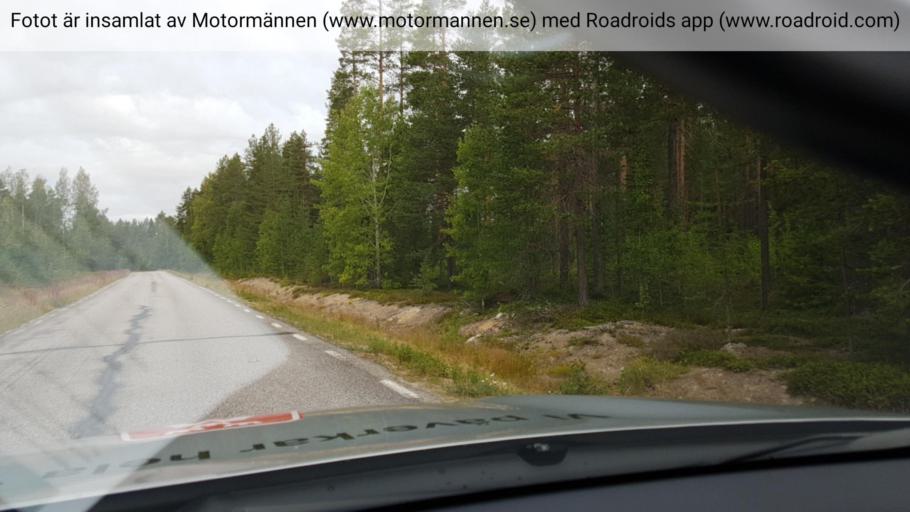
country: SE
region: Norrbotten
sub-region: Bodens Kommun
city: Saevast
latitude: 65.6709
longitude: 21.7053
